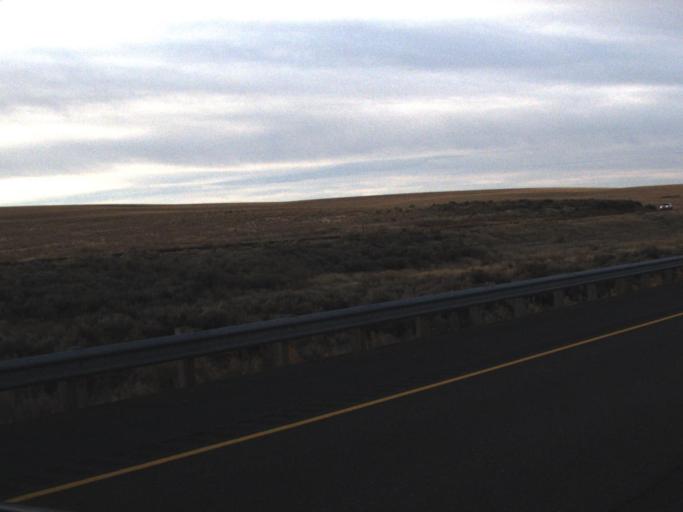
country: US
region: Washington
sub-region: Adams County
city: Ritzville
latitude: 46.9173
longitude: -118.6034
